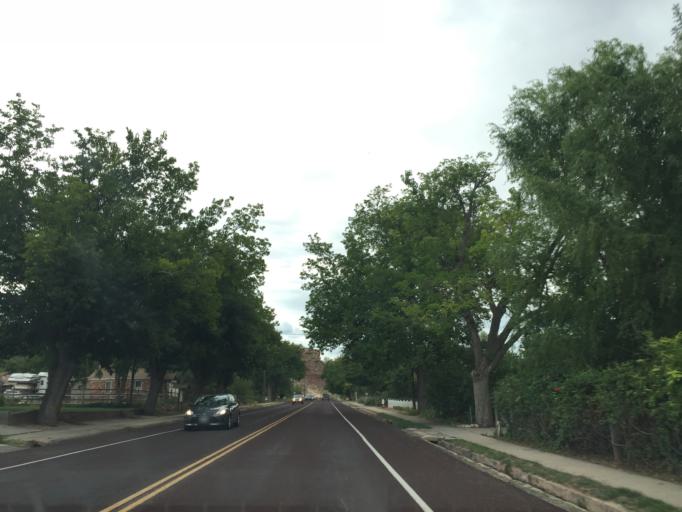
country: US
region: Utah
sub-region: Washington County
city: Hildale
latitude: 37.1612
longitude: -113.0392
